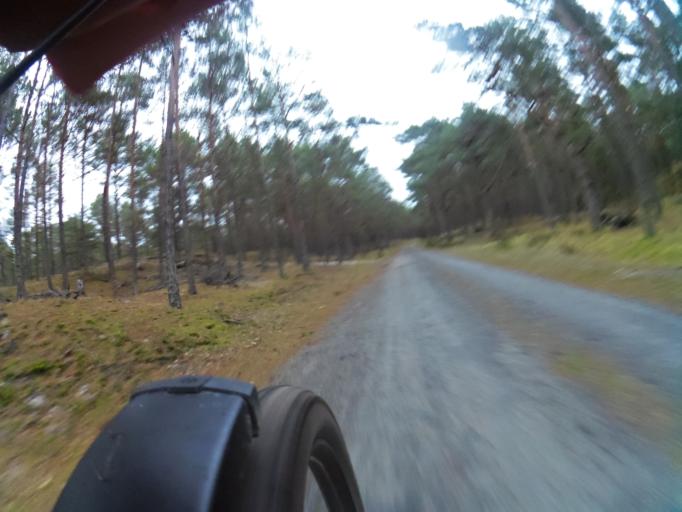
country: PL
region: Pomeranian Voivodeship
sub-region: Powiat wejherowski
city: Choczewo
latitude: 54.7880
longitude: 17.7495
